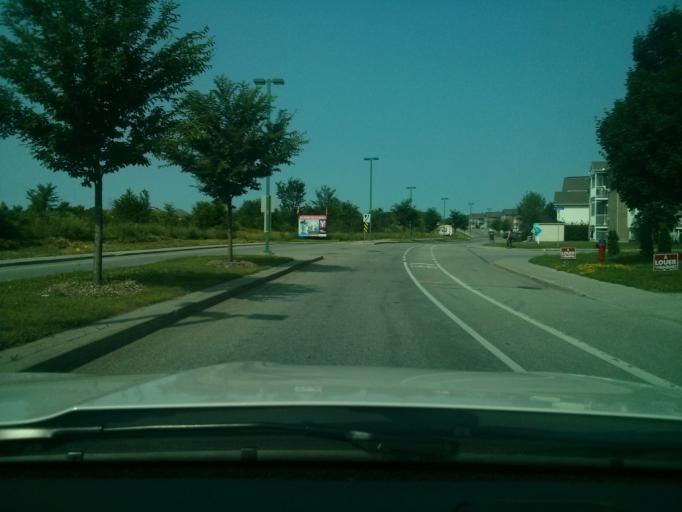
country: CA
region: Ontario
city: Ottawa
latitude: 45.4332
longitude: -75.7862
